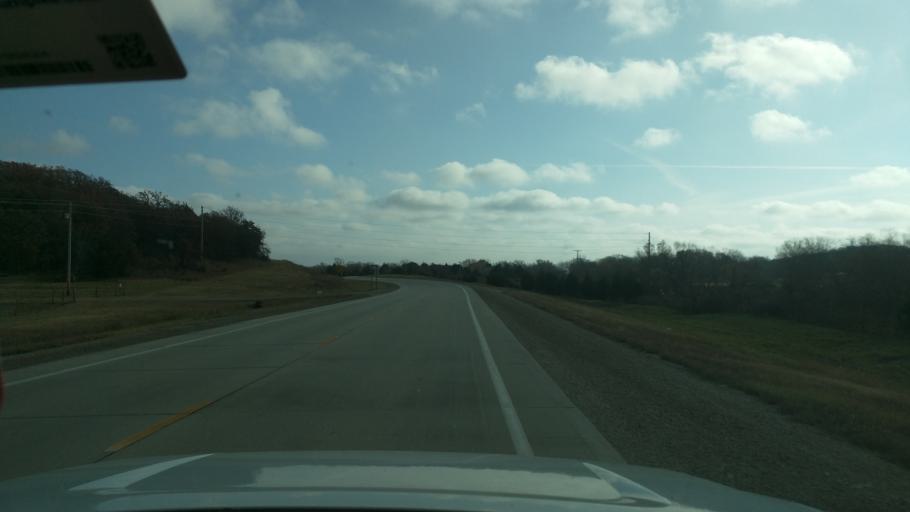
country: US
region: Kansas
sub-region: Montgomery County
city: Caney
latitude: 37.0675
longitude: -96.0227
